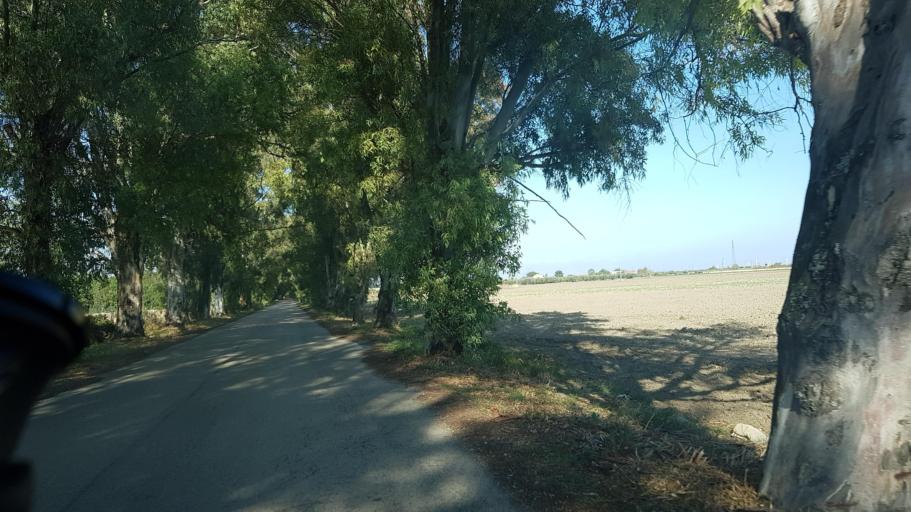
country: IT
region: Apulia
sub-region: Provincia di Foggia
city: Carapelle
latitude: 41.3905
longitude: 15.6507
